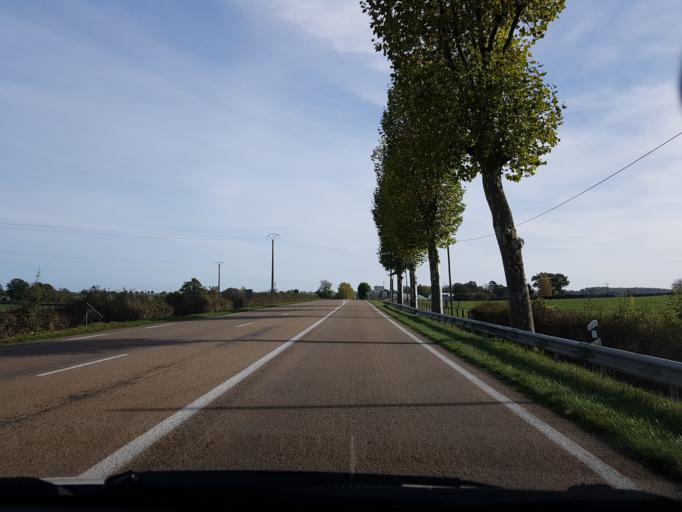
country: FR
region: Bourgogne
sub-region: Departement de l'Yonne
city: Avallon
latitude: 47.4764
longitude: 4.0135
